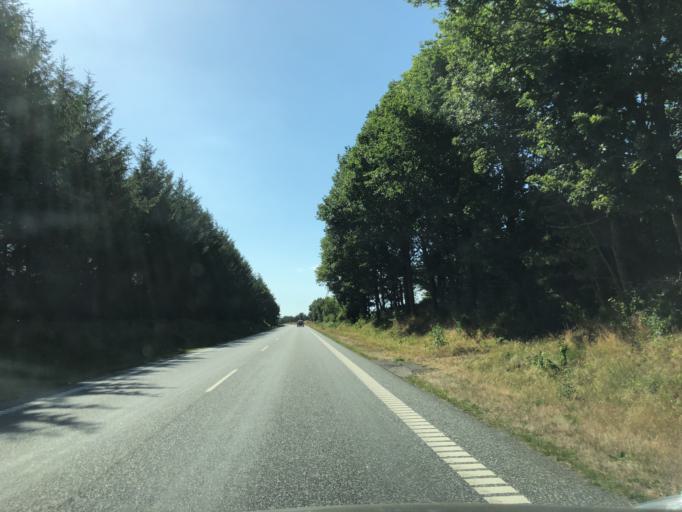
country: DK
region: North Denmark
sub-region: Vesthimmerland Kommune
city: Alestrup
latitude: 56.6122
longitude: 9.3910
